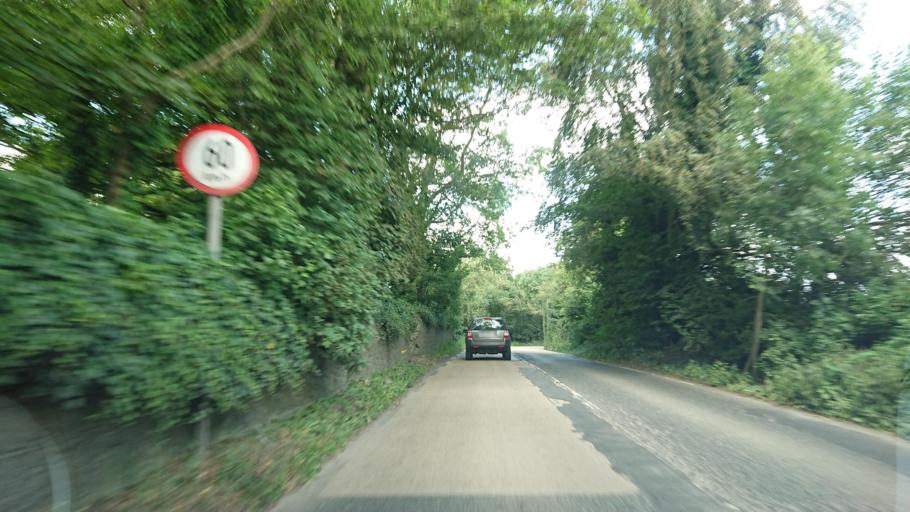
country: IE
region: Leinster
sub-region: Kildare
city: Sallins
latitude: 53.2669
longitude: -6.6706
